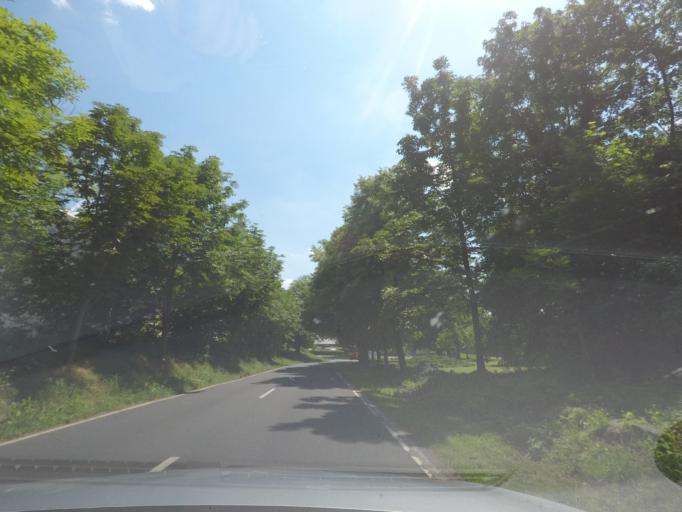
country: DE
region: Saxony-Anhalt
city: Haldensleben I
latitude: 52.2492
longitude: 11.4063
